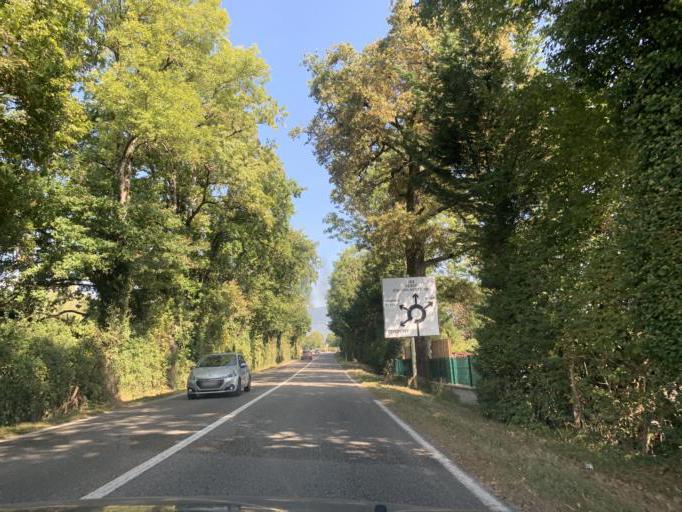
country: FR
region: Rhone-Alpes
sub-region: Departement de l'Ain
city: Echenevex
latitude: 46.3088
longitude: 6.0484
